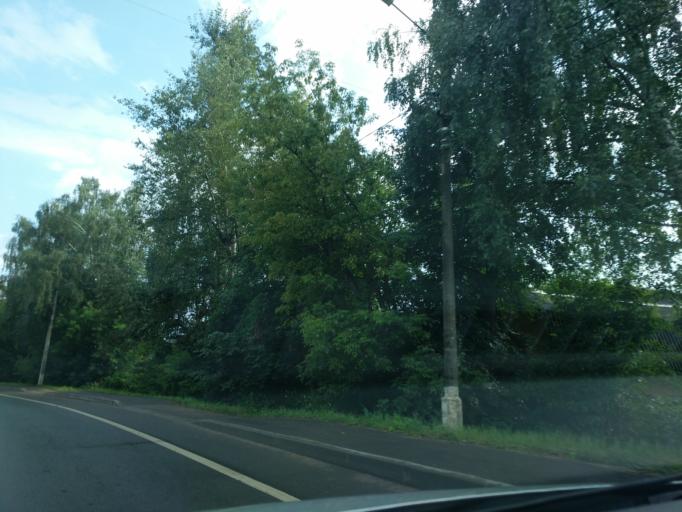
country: RU
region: Moskovskaya
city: Lobnya
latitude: 56.0115
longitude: 37.5053
